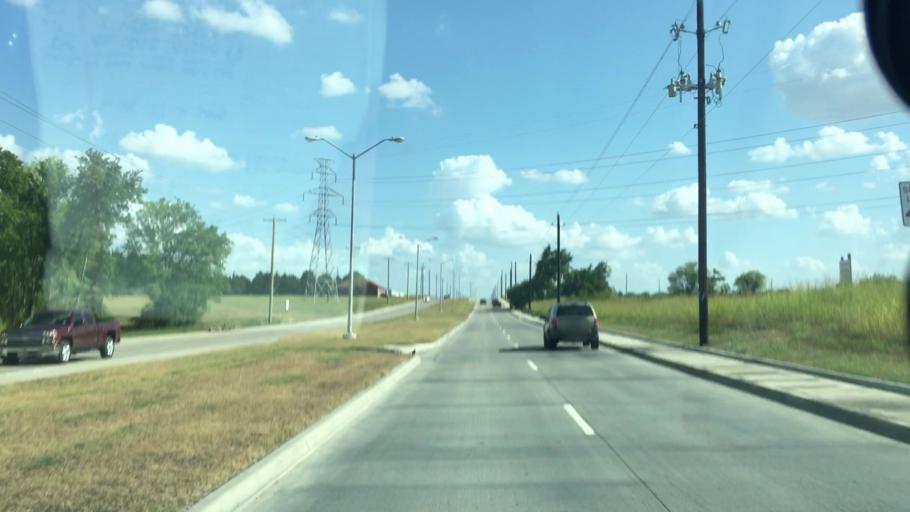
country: US
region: Texas
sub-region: Dallas County
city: Hutchins
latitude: 32.6401
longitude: -96.7518
